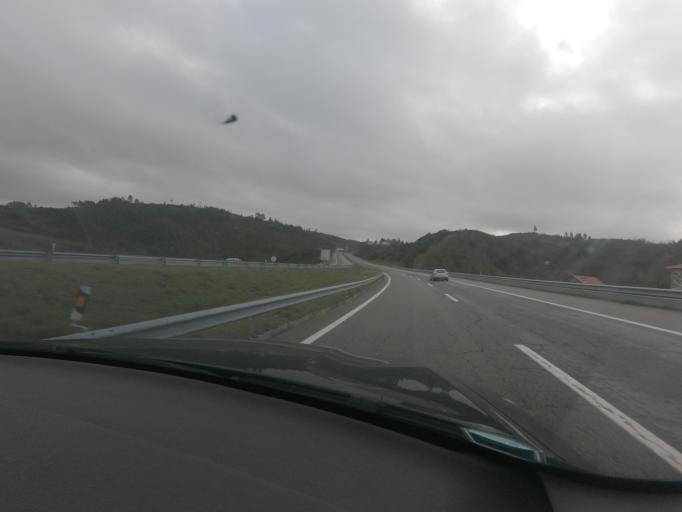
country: PT
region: Viseu
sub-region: Castro Daire
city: Castro Daire
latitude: 40.8870
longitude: -7.9210
